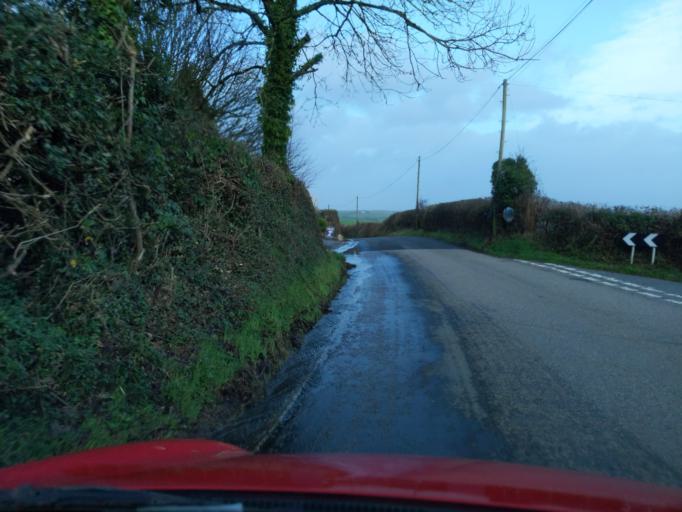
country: GB
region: England
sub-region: Devon
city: Great Torrington
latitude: 50.9221
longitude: -4.1979
